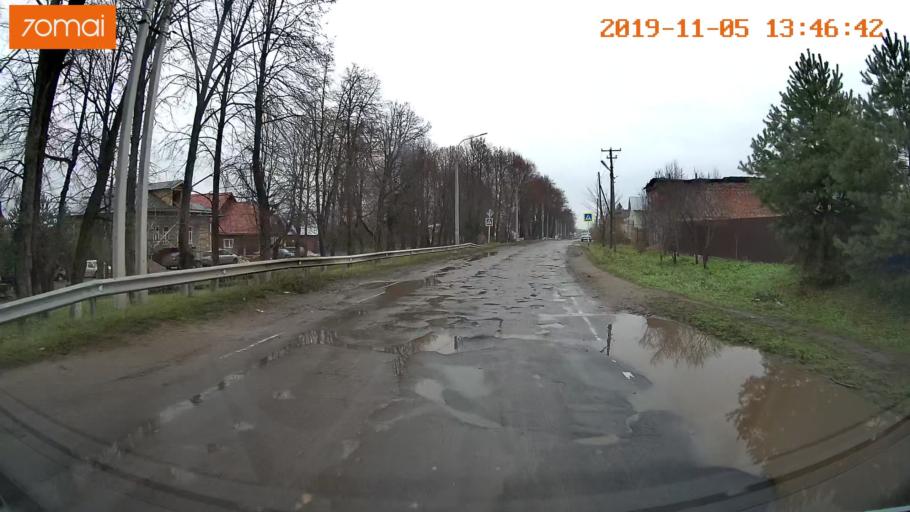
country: RU
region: Ivanovo
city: Shuya
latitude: 56.9968
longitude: 41.4098
